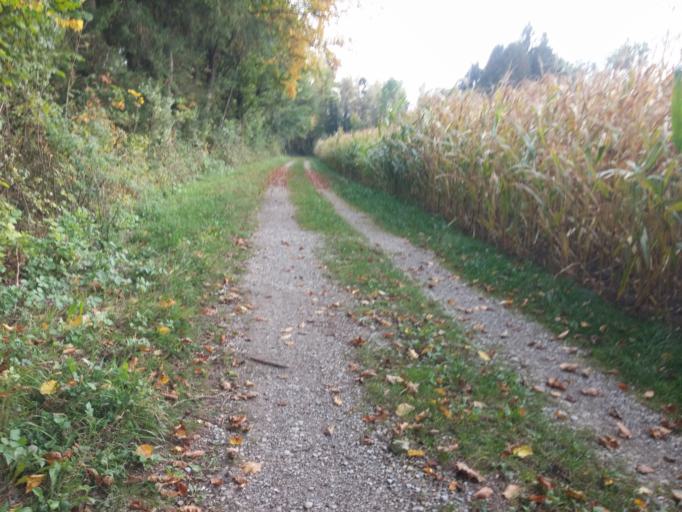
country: DE
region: Baden-Wuerttemberg
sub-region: Tuebingen Region
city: Aitrach
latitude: 47.9342
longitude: 10.1098
